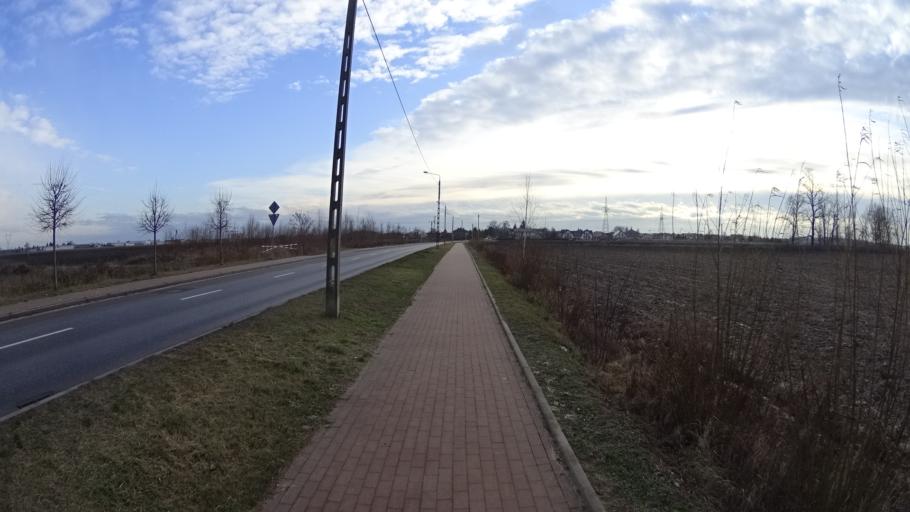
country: PL
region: Masovian Voivodeship
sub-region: Powiat warszawski zachodni
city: Ozarow Mazowiecki
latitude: 52.2296
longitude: 20.8023
